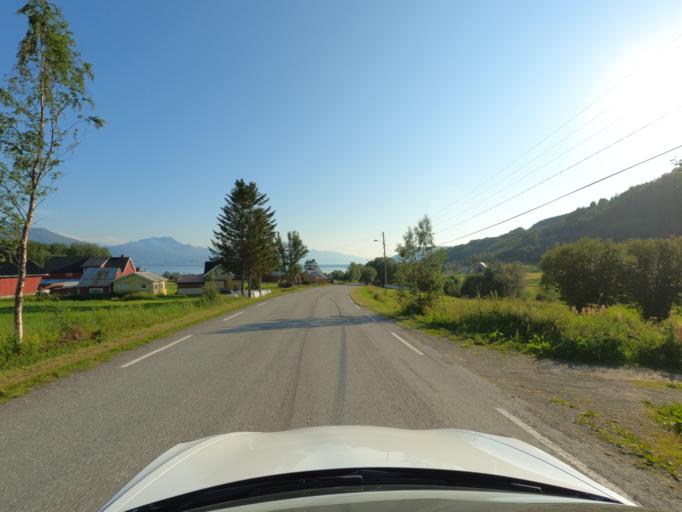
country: NO
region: Nordland
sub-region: Narvik
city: Bjerkvik
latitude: 68.5328
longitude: 17.4765
